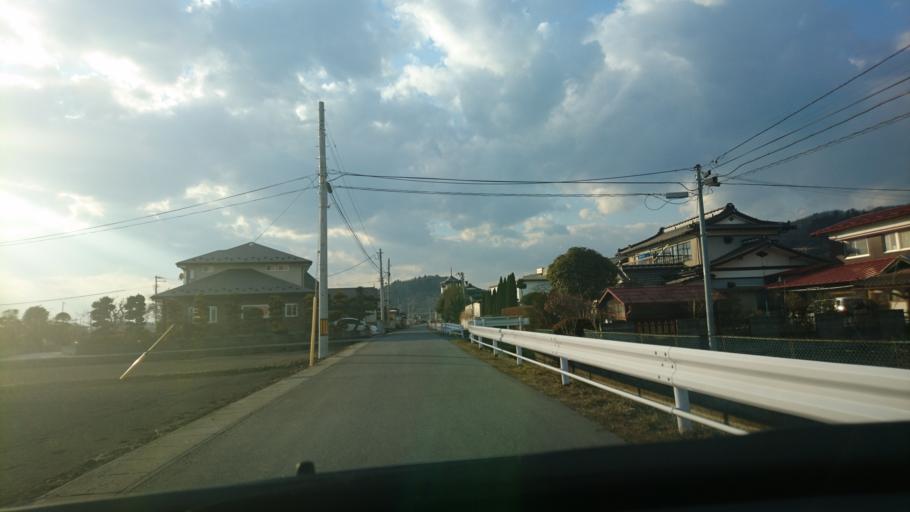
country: JP
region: Iwate
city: Ichinoseki
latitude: 38.9398
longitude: 141.0863
